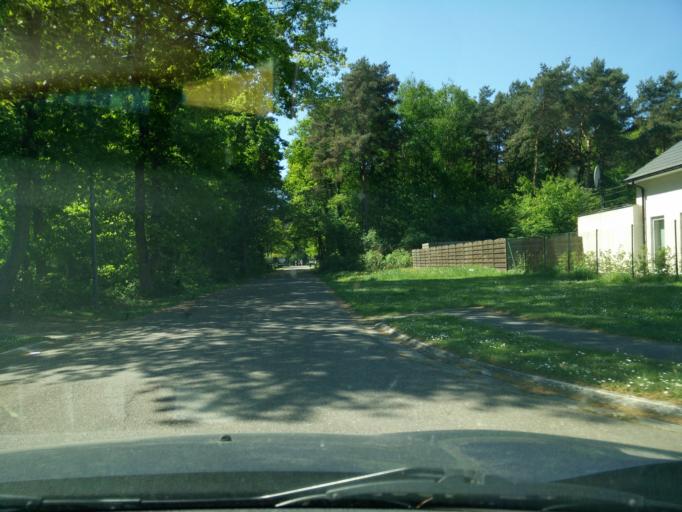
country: BE
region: Flanders
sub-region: Provincie Limburg
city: Maasmechelen
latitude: 50.9896
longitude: 5.6786
